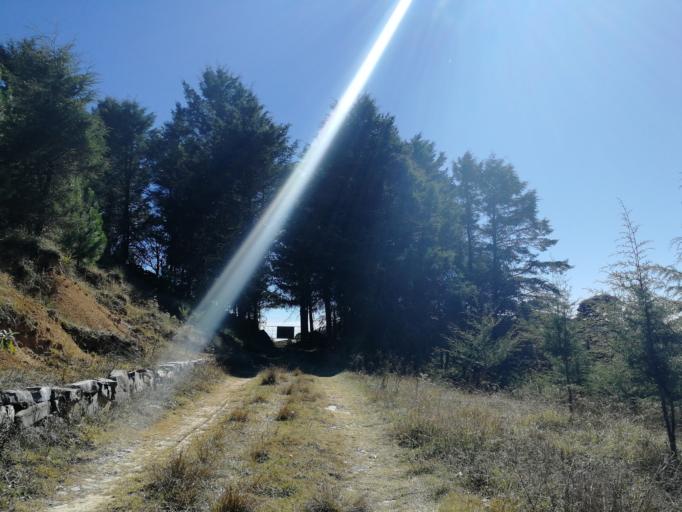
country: MX
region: San Luis Potosi
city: Zaragoza
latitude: 22.0127
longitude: -100.6199
